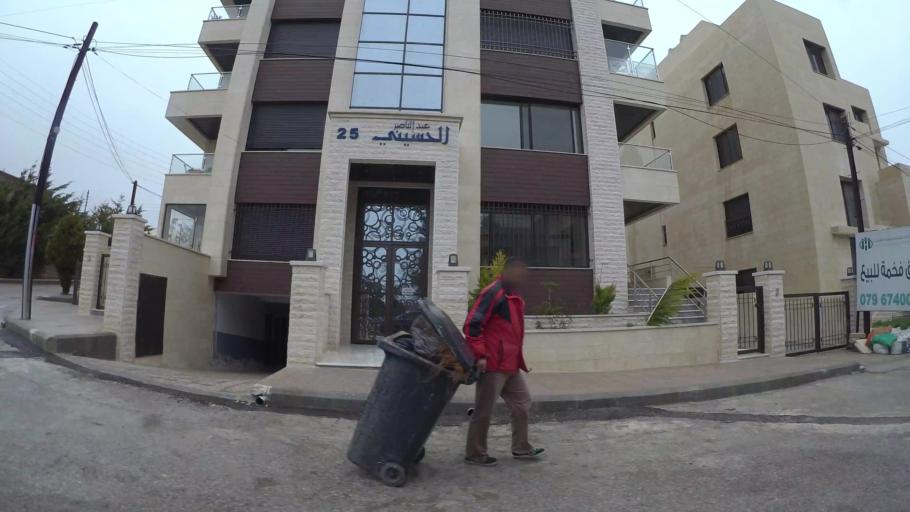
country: JO
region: Amman
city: Wadi as Sir
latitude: 31.9672
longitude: 35.8469
